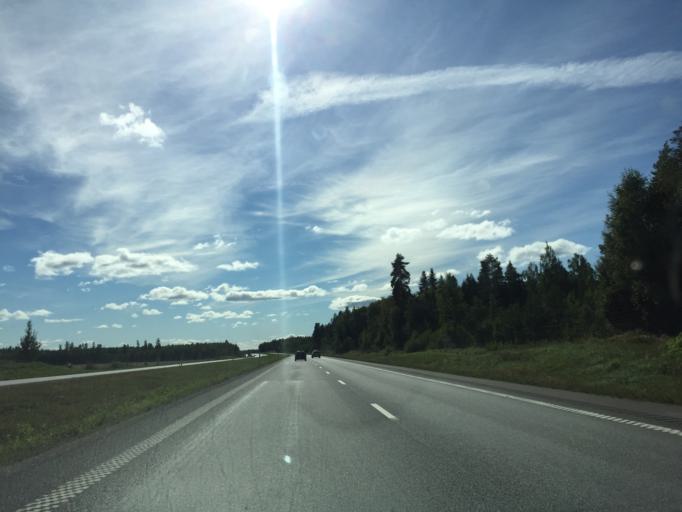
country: SE
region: Vaestmanland
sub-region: Kopings Kommun
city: Koping
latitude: 59.4732
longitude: 15.9039
